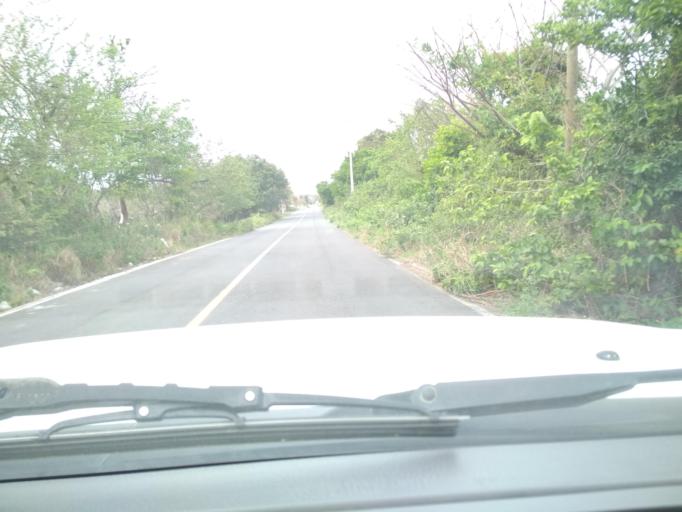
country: MX
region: Veracruz
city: Anton Lizardo
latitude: 19.0461
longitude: -95.9866
